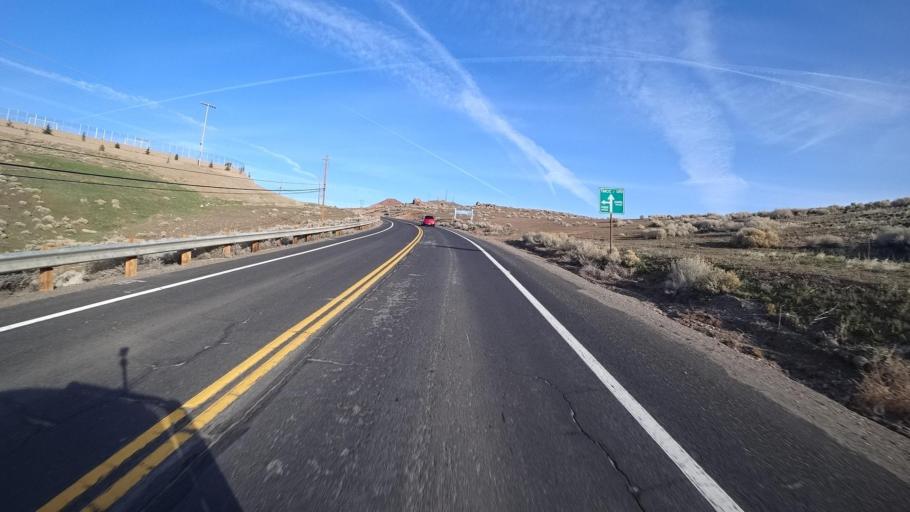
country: US
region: Nevada
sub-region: Washoe County
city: Sun Valley
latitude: 39.5731
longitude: -119.7889
